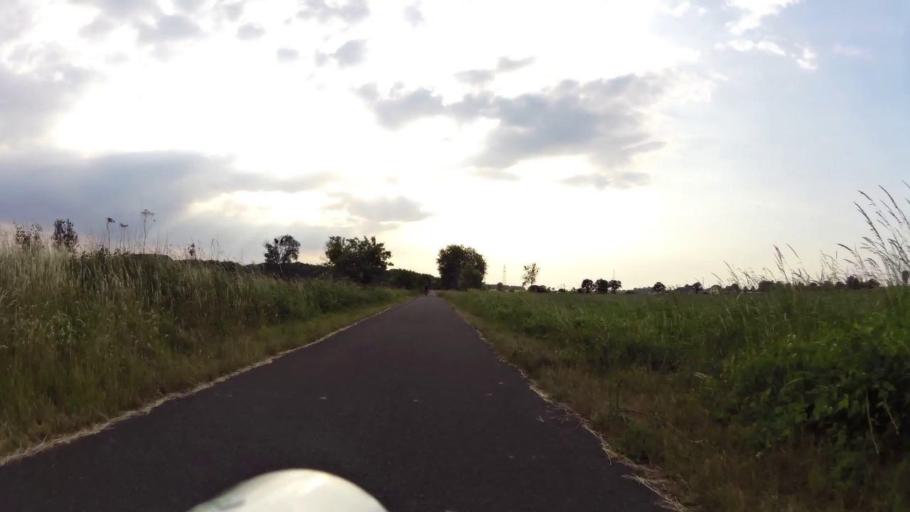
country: PL
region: Kujawsko-Pomorskie
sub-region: Powiat chelminski
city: Unislaw
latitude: 53.1815
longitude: 18.4000
